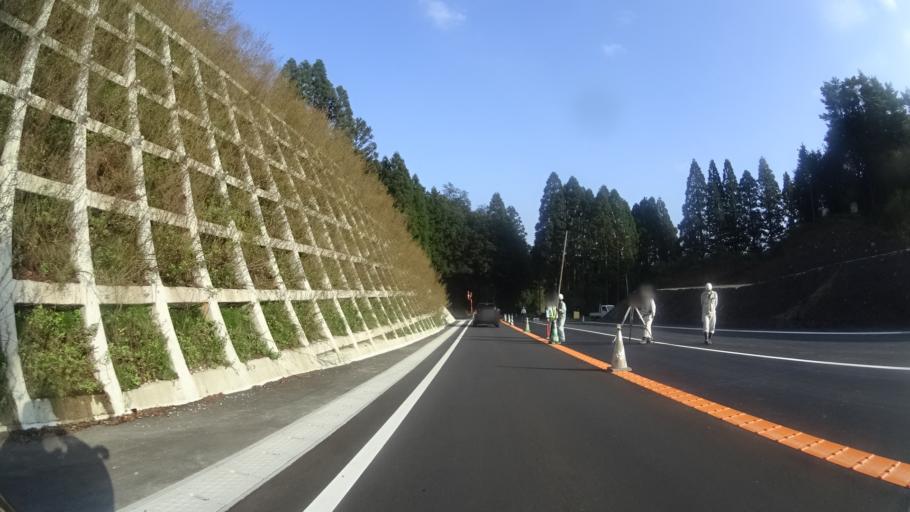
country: JP
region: Oita
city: Beppu
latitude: 33.2703
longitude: 131.4348
